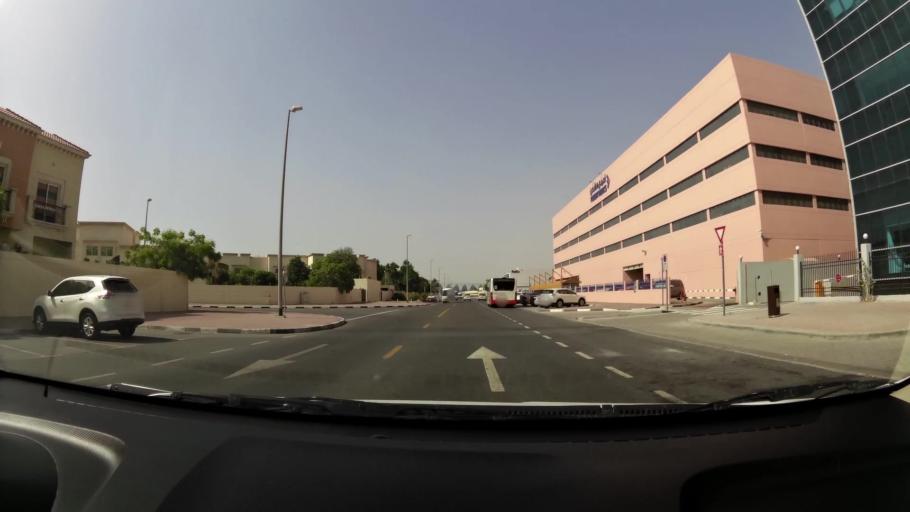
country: AE
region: Ash Shariqah
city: Sharjah
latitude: 25.2376
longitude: 55.3578
